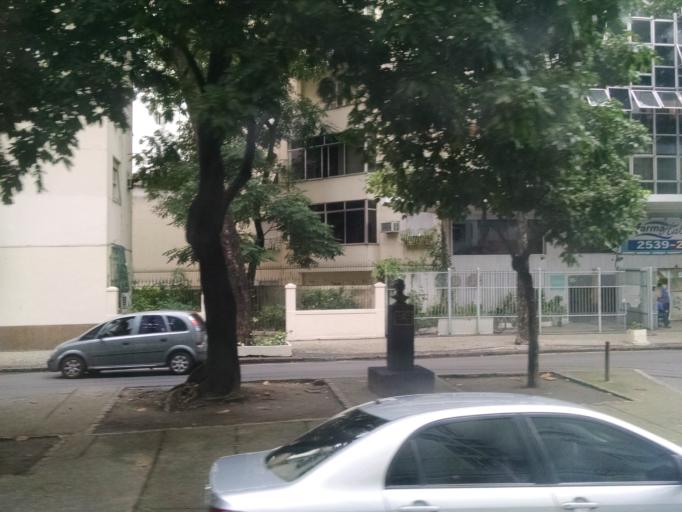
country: BR
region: Rio de Janeiro
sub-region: Rio De Janeiro
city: Rio de Janeiro
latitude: -22.9557
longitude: -43.1979
